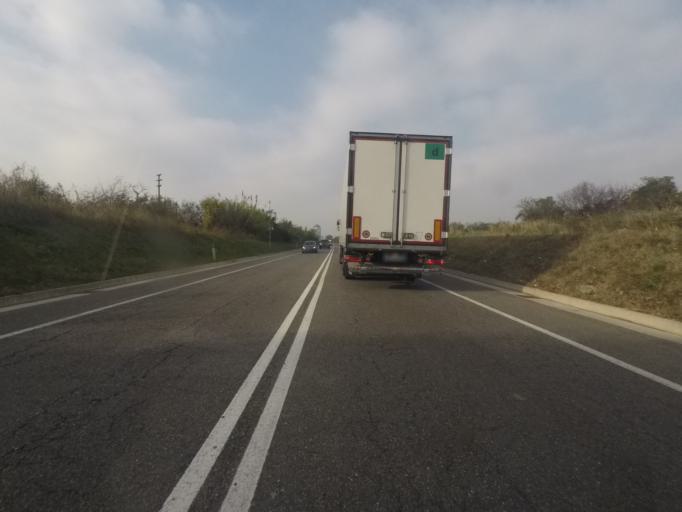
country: IT
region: Lombardy
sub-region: Provincia di Monza e Brianza
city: Burago di Molgora
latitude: 45.6060
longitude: 9.3786
